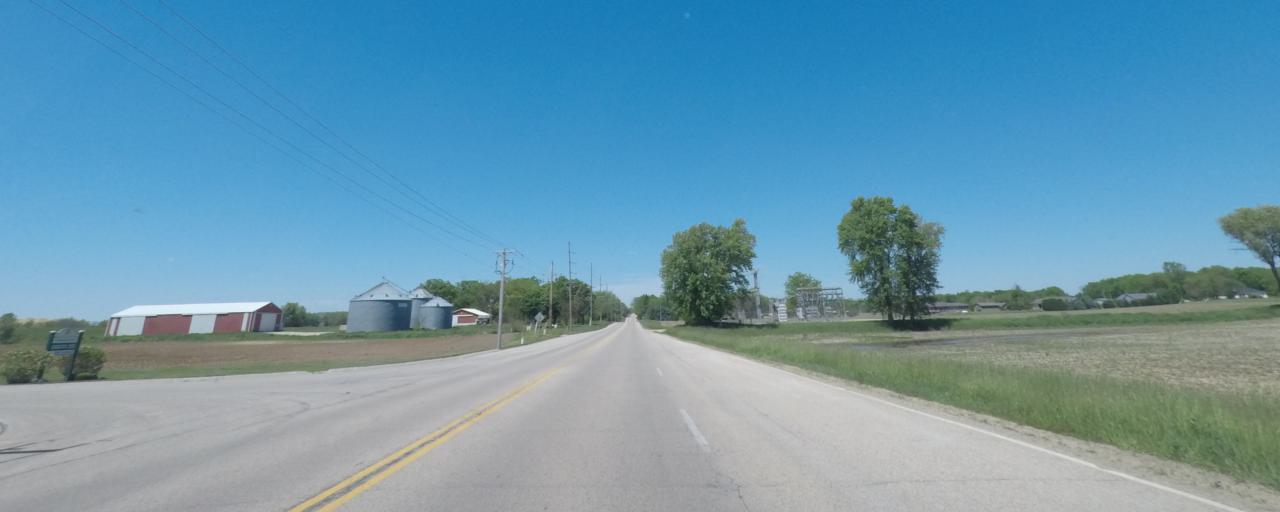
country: US
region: Wisconsin
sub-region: Green County
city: Brooklyn
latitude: 42.8624
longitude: -89.3691
